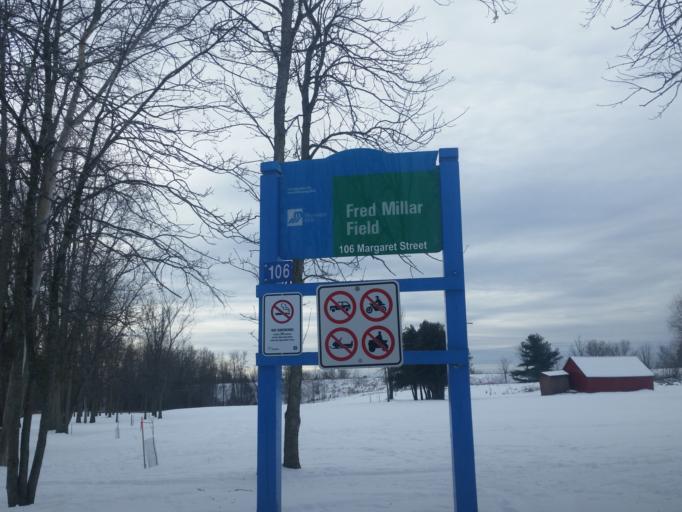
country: CA
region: Ontario
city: Arnprior
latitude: 45.3295
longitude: -76.2891
